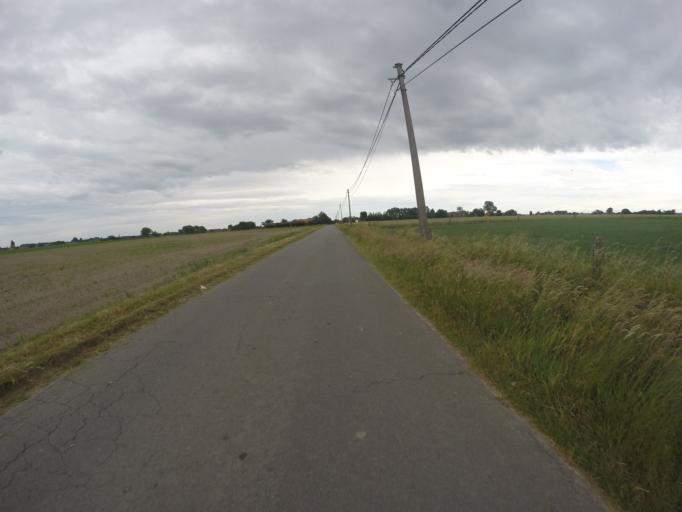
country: BE
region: Flanders
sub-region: Provincie West-Vlaanderen
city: Ruiselede
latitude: 51.0484
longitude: 3.3540
